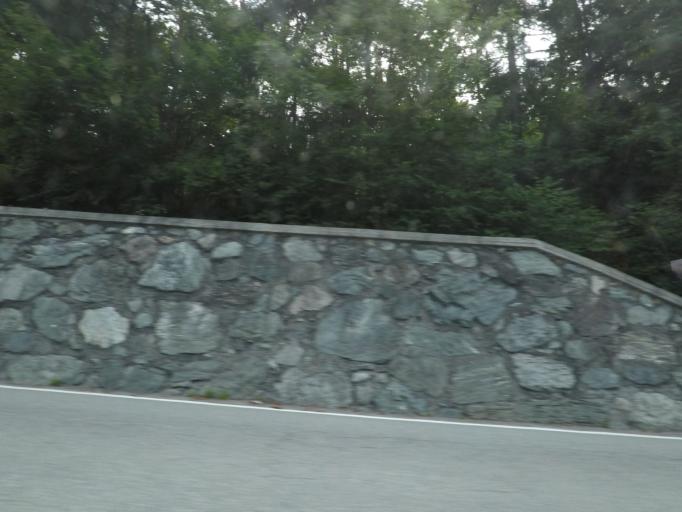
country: IT
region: Aosta Valley
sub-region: Valle d'Aosta
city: Antey-Saint-Andre
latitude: 45.7921
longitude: 7.5901
